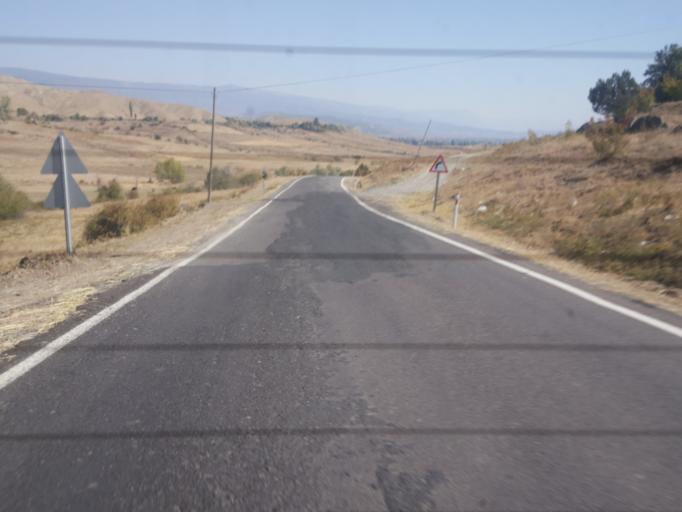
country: TR
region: Kastamonu
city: Tosya
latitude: 40.9849
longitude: 34.0799
